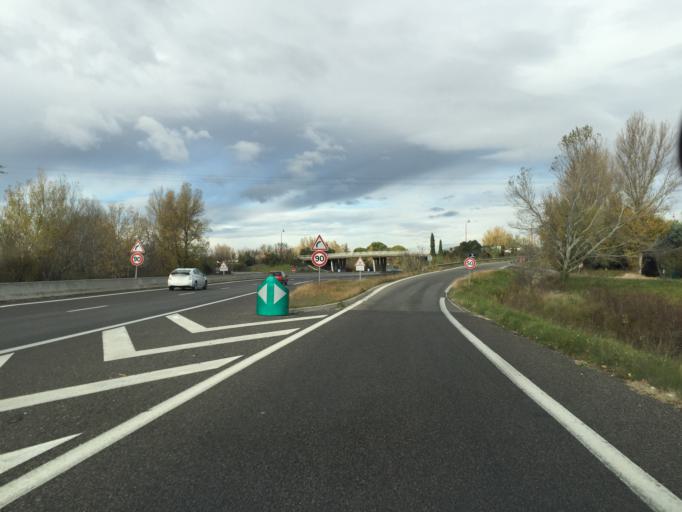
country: FR
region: Provence-Alpes-Cote d'Azur
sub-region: Departement du Vaucluse
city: Althen-des-Paluds
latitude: 44.0054
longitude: 4.9414
